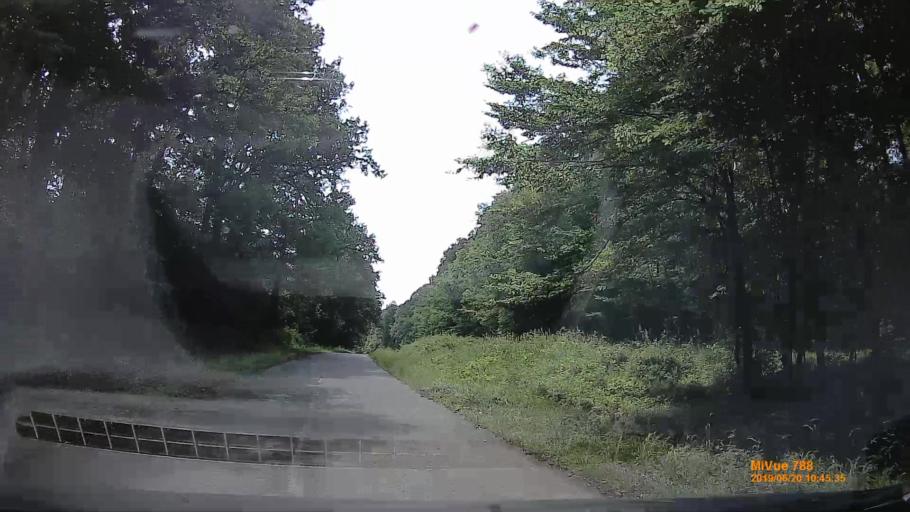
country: HU
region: Baranya
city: Hidas
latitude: 46.1823
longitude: 18.5720
